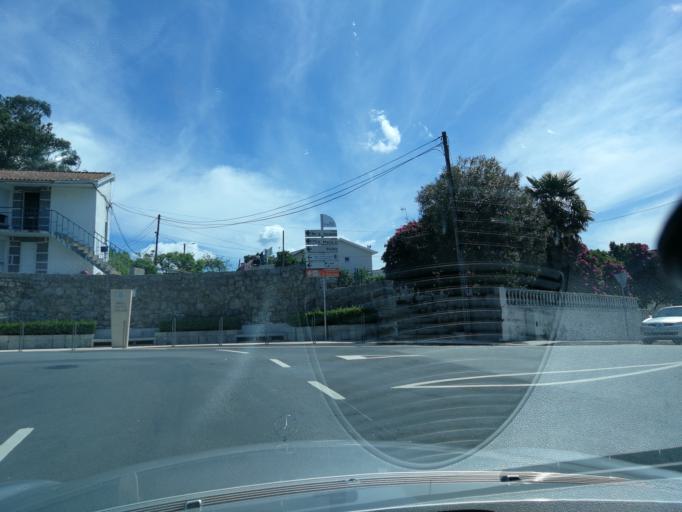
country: PT
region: Braga
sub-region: Vila Nova de Famalicao
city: Vila Nova de Famalicao
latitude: 41.4145
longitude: -8.5164
